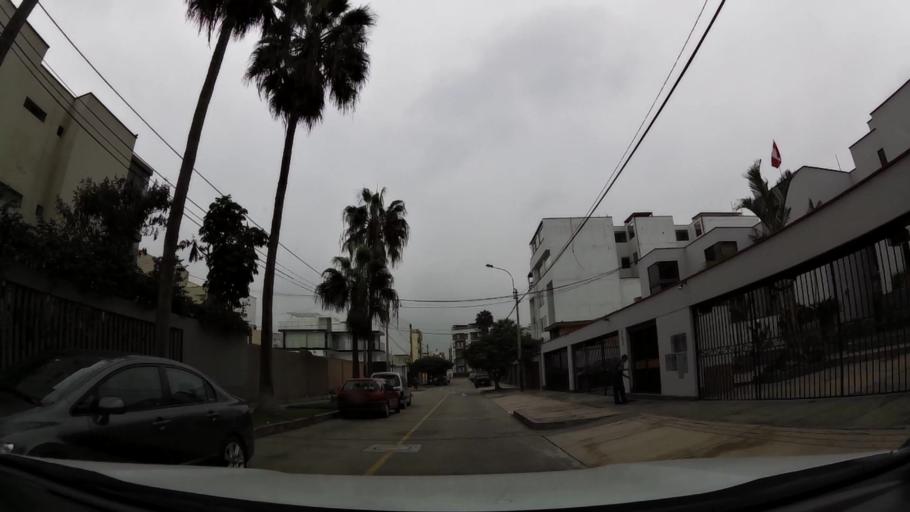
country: PE
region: Lima
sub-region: Lima
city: Surco
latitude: -12.1342
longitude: -77.0087
